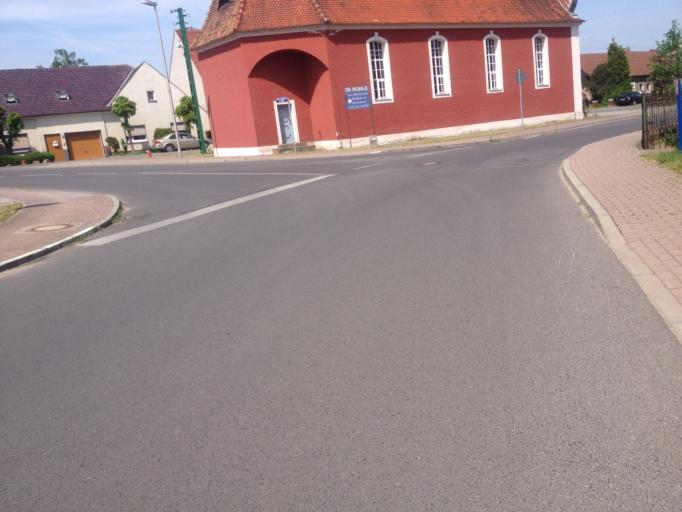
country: DE
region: Brandenburg
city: Drehnow
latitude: 51.8181
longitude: 14.3411
